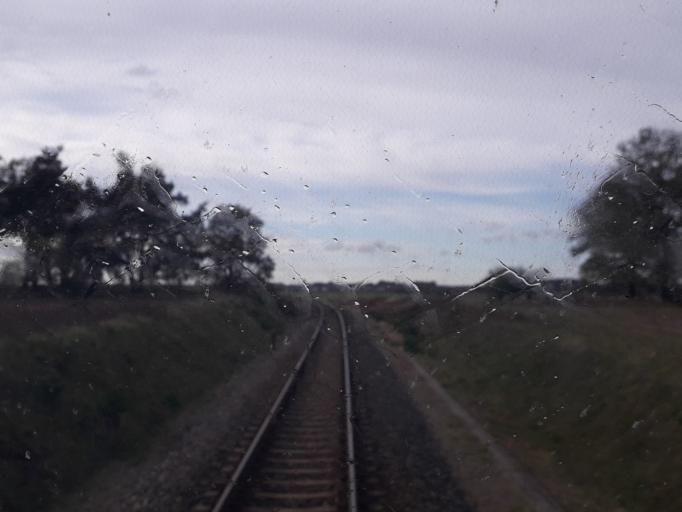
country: DE
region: Brandenburg
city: Wittstock
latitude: 53.1585
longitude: 12.4360
